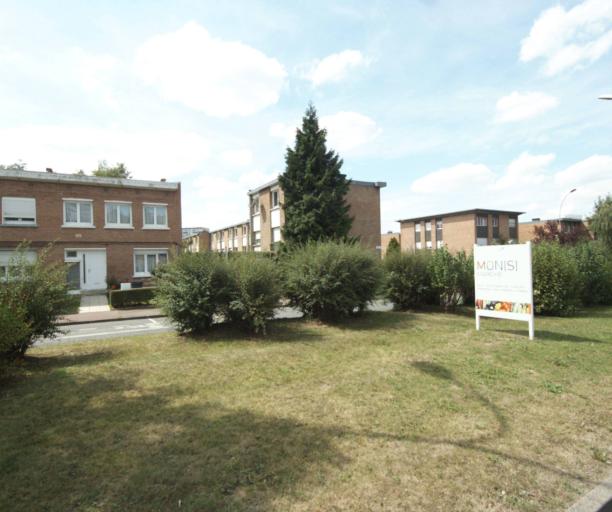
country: FR
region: Nord-Pas-de-Calais
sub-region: Departement du Nord
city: Mons-en-Baroeul
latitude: 50.6391
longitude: 3.1145
